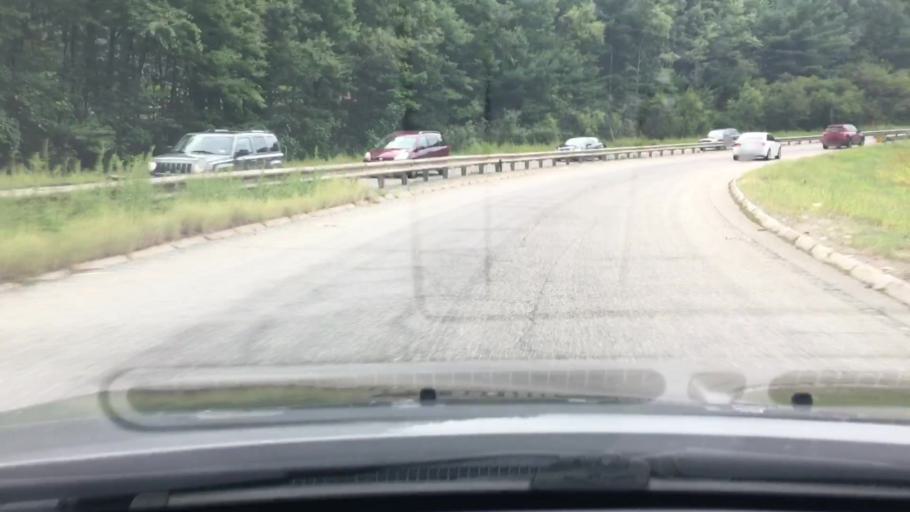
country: US
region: Massachusetts
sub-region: Worcester County
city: Cordaville
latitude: 42.2639
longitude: -71.5612
